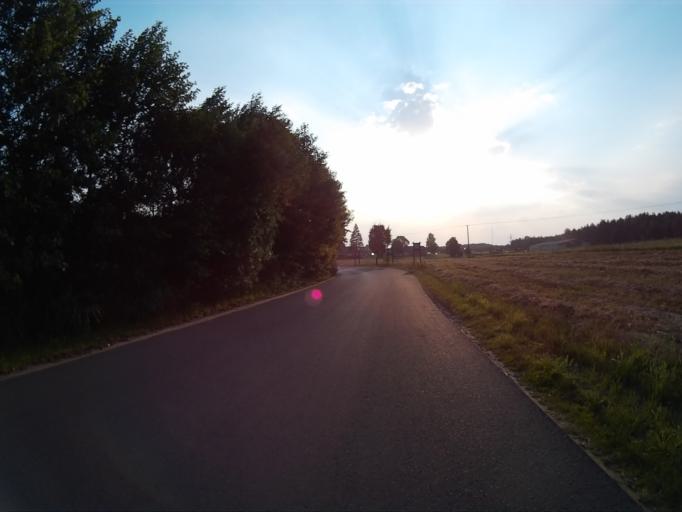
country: PL
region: Pomeranian Voivodeship
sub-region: Powiat chojnicki
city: Czersk
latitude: 53.7230
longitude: 17.9185
